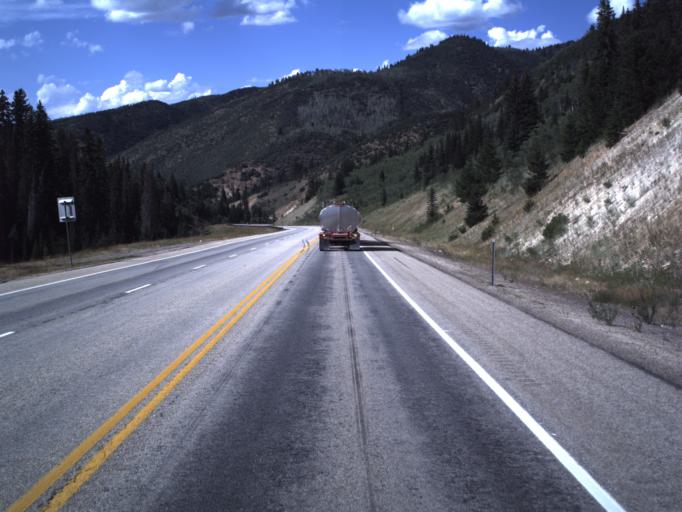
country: US
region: Utah
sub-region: Wasatch County
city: Heber
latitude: 40.3296
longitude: -111.2608
